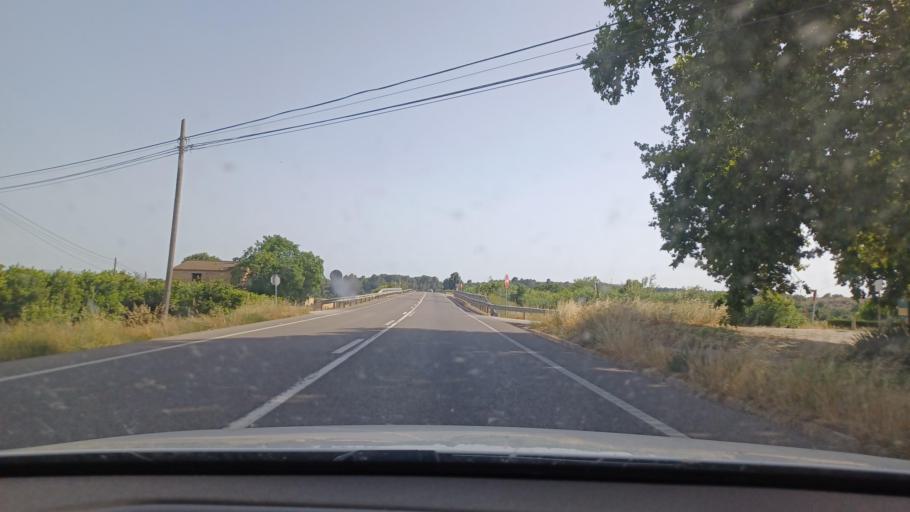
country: ES
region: Catalonia
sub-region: Provincia de Tarragona
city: Tortosa
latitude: 40.7945
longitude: 0.4975
